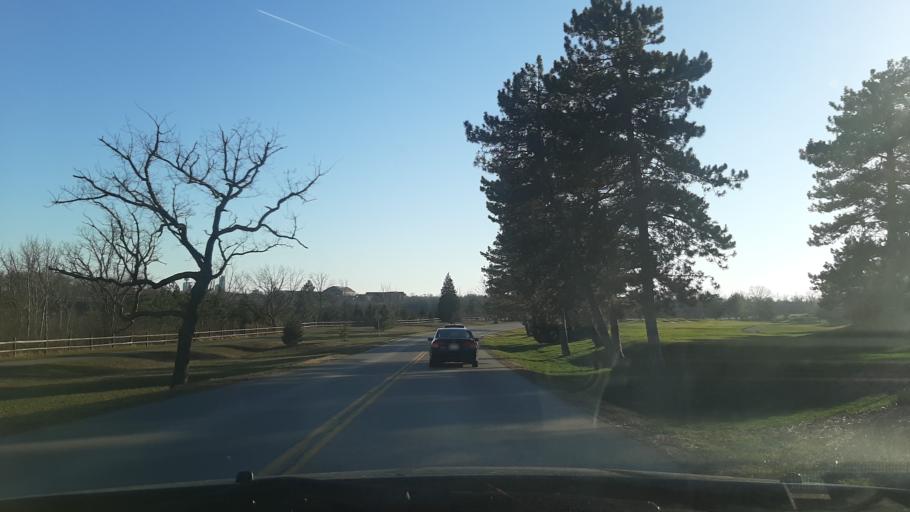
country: CA
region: Ontario
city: Niagara Falls
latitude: 43.1268
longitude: -79.0635
